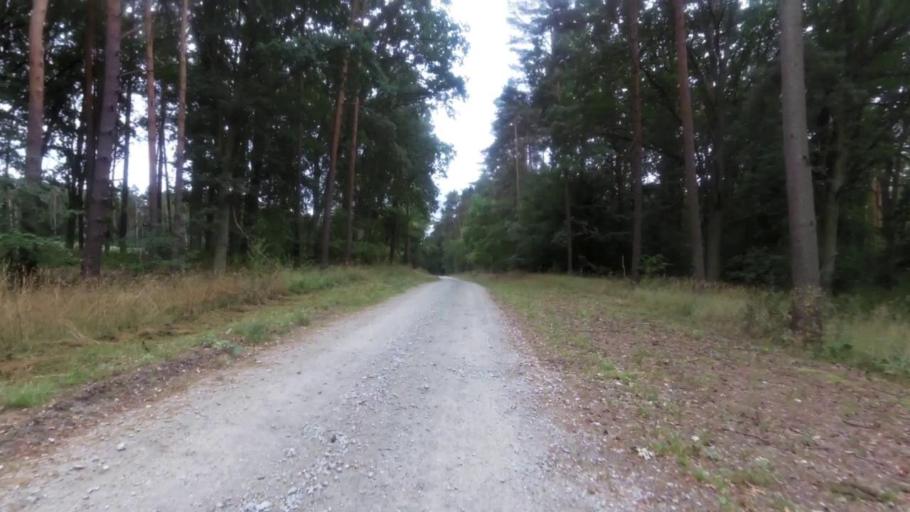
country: PL
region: Lubusz
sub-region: Powiat gorzowski
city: Kostrzyn nad Odra
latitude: 52.6302
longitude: 14.6487
